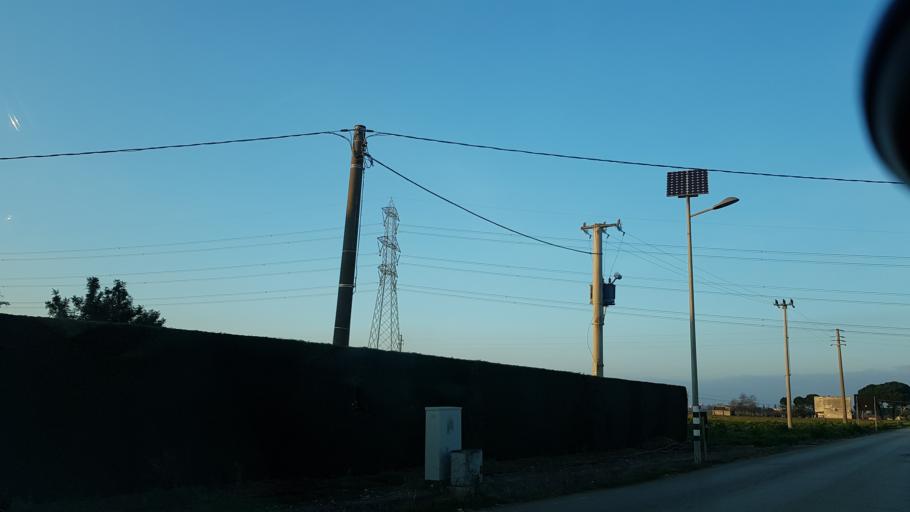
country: IT
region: Apulia
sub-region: Provincia di Brindisi
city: La Rosa
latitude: 40.5910
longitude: 17.9441
